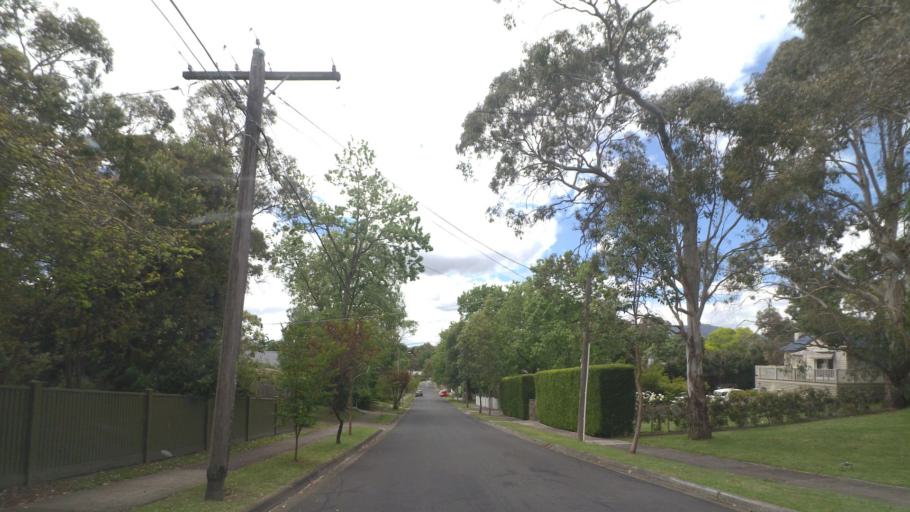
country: AU
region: Victoria
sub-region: Maroondah
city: Croydon North
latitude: -37.7930
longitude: 145.2936
